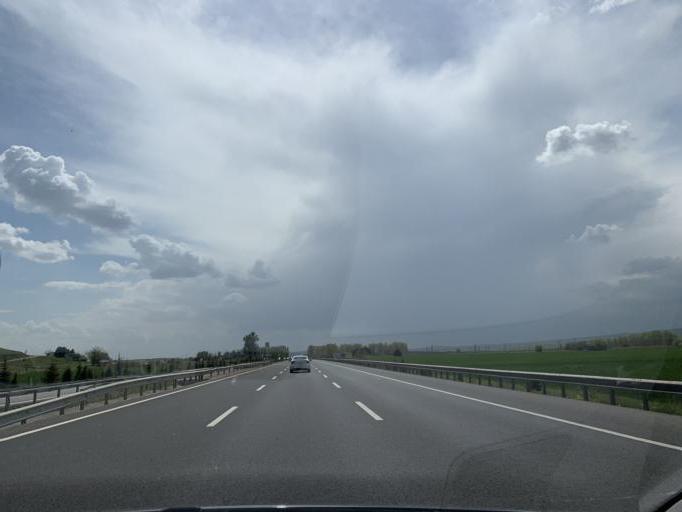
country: TR
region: Ankara
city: Temelli
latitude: 39.6985
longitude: 32.2655
